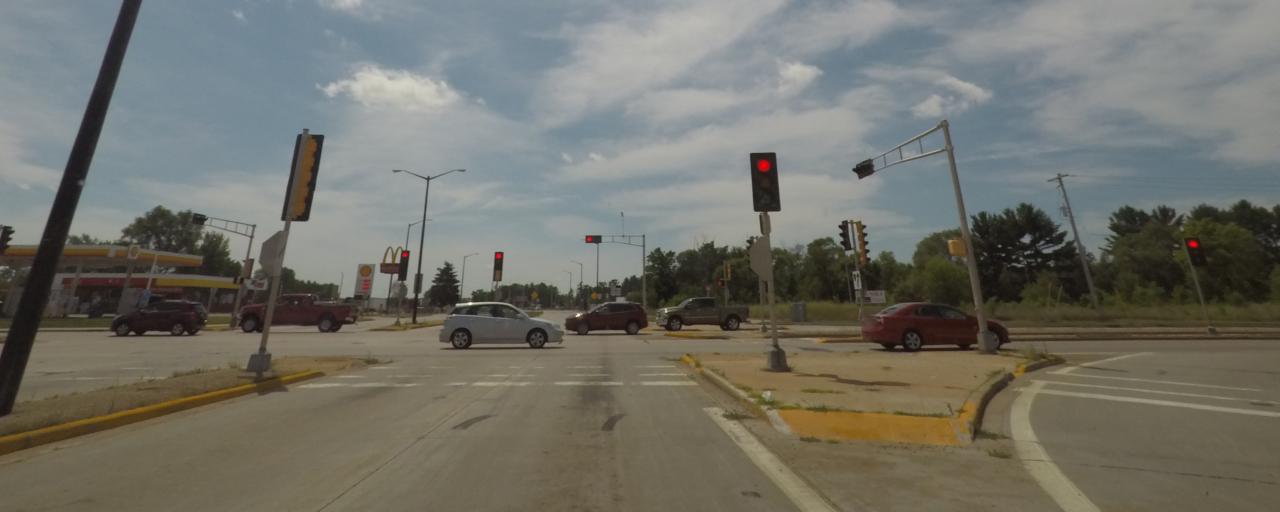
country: US
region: Wisconsin
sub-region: Portage County
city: Plover
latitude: 44.4540
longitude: -89.5442
